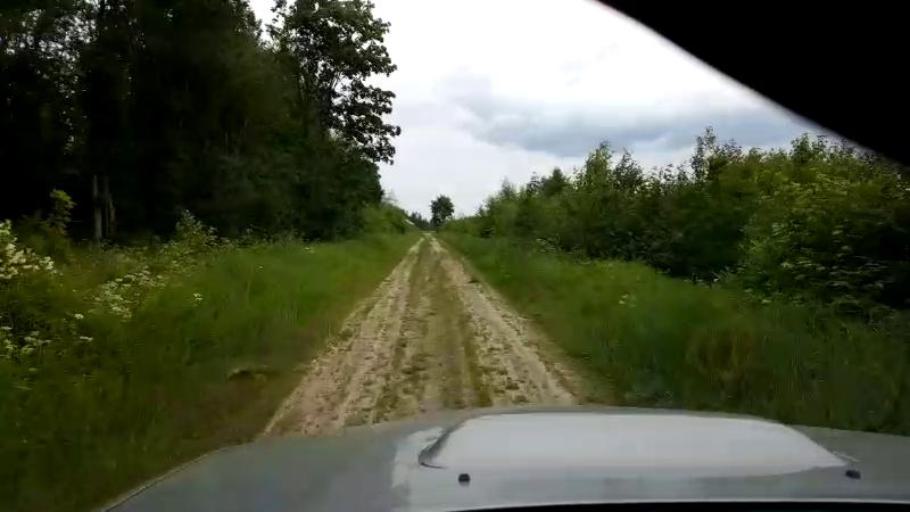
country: EE
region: Paernumaa
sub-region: Halinga vald
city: Parnu-Jaagupi
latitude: 58.5357
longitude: 24.6169
